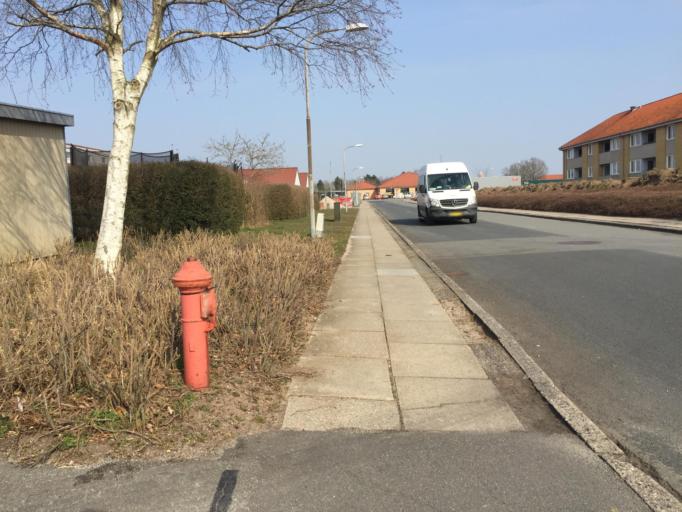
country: DK
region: South Denmark
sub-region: Kerteminde Kommune
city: Langeskov
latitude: 55.3589
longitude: 10.5847
